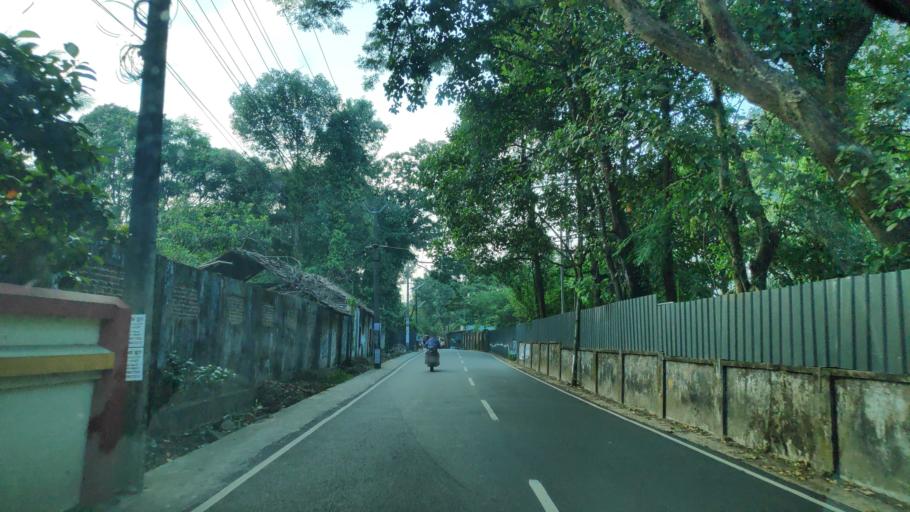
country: IN
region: Kerala
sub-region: Alappuzha
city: Shertallai
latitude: 9.6779
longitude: 76.3914
